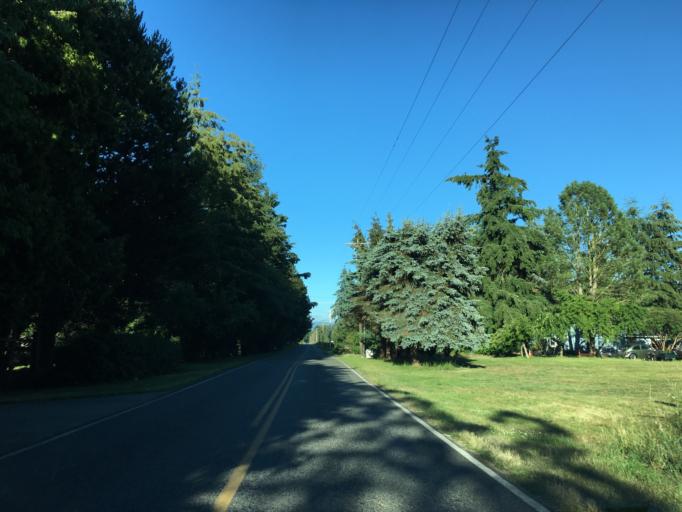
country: US
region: Washington
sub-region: Whatcom County
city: Ferndale
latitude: 48.9135
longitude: -122.6197
